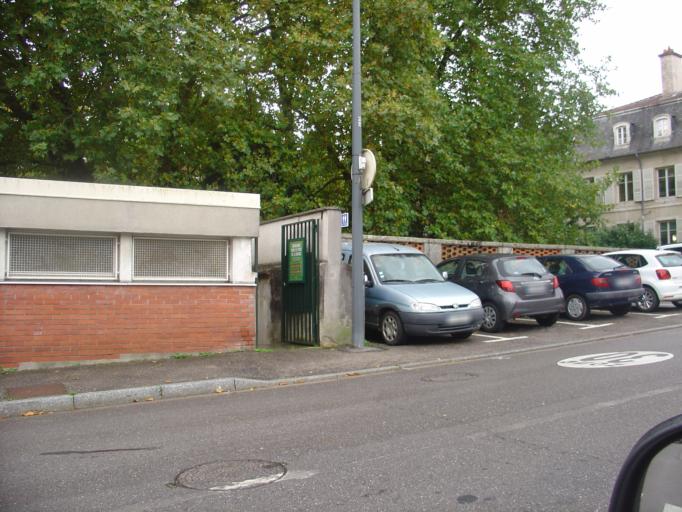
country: FR
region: Lorraine
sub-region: Departement de Meurthe-et-Moselle
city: Maxeville
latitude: 48.7125
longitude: 6.1638
